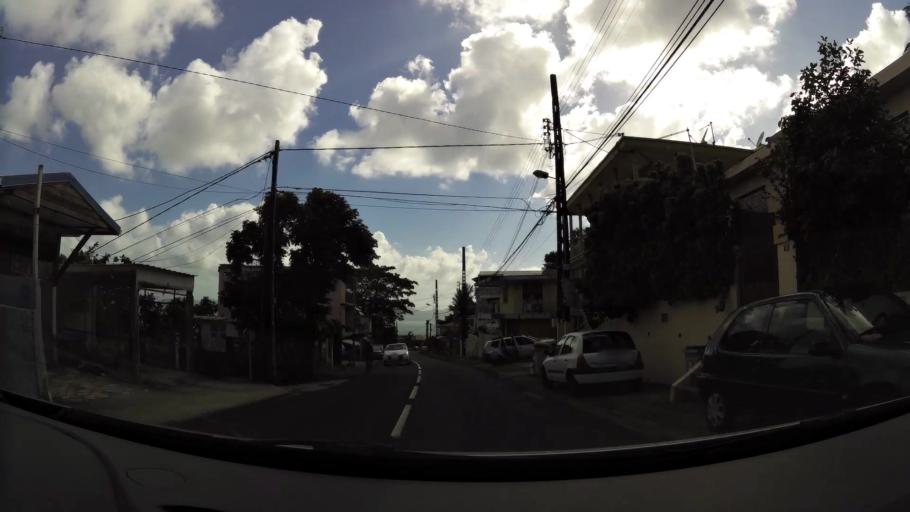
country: MQ
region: Martinique
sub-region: Martinique
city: Fort-de-France
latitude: 14.6202
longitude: -61.0607
